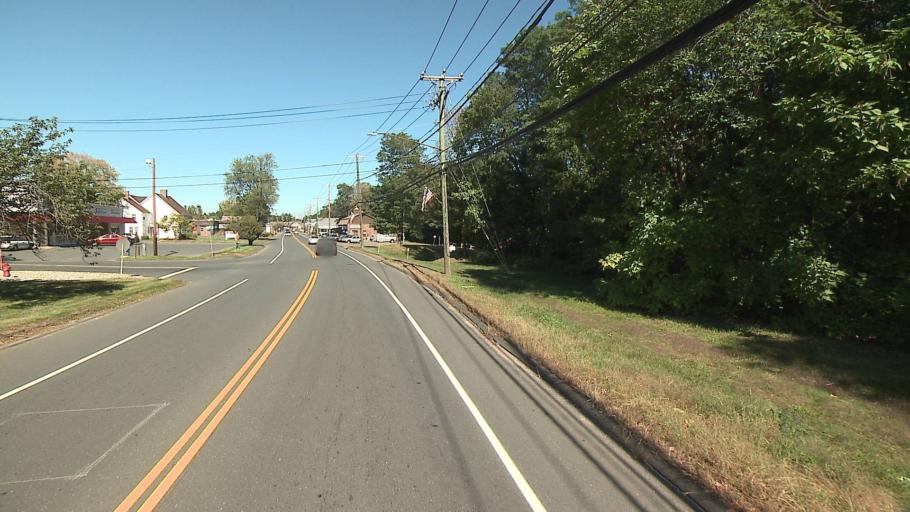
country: US
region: Connecticut
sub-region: Hartford County
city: Tariffville
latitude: 41.8988
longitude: -72.7866
